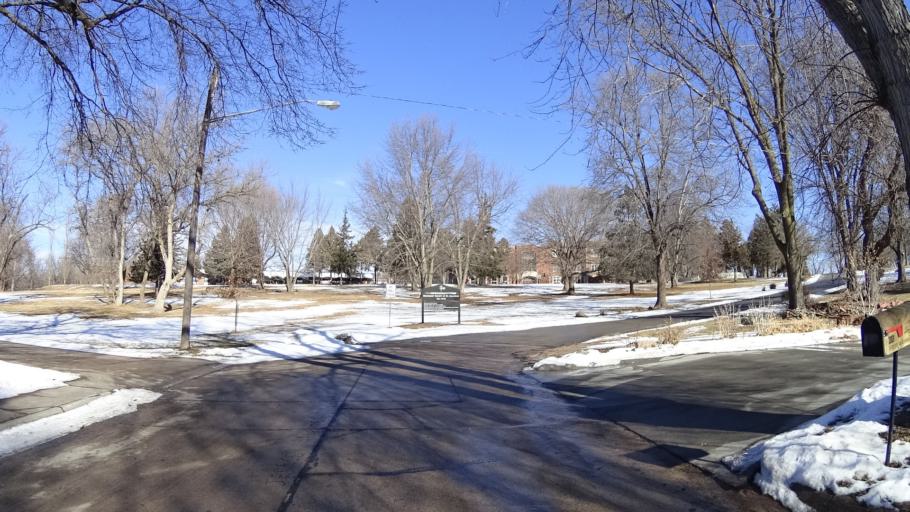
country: US
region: Nebraska
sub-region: Sarpy County
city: Bellevue
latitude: 41.1393
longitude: -95.9042
